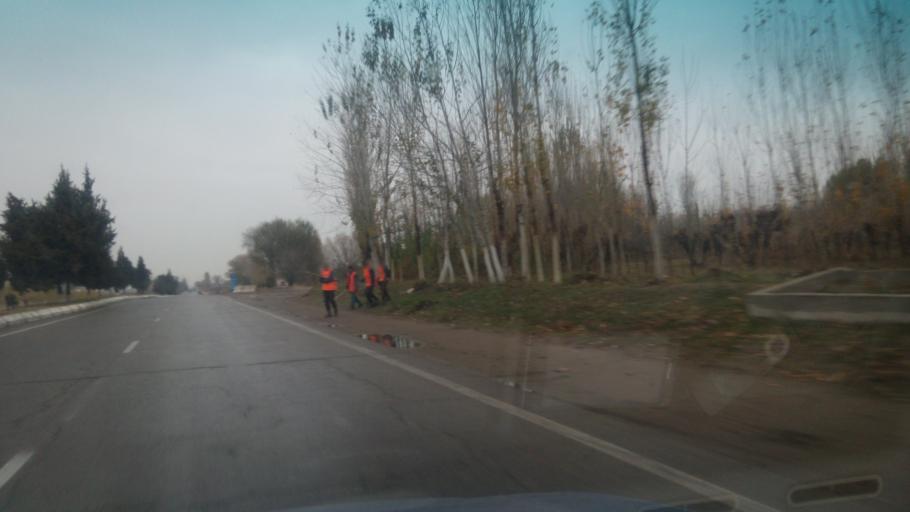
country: UZ
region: Toshkent
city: Zafar
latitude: 41.0403
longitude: 68.8809
